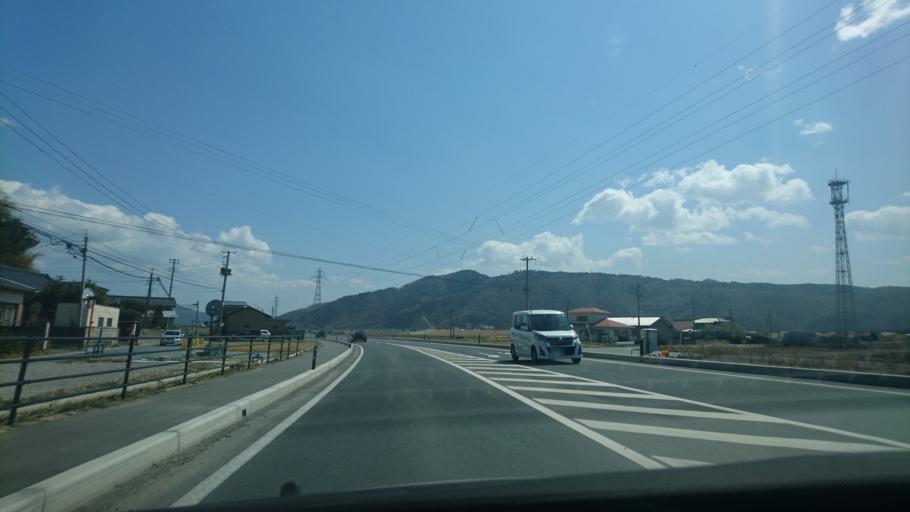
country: JP
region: Miyagi
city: Ishinomaki
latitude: 38.4504
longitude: 141.3183
